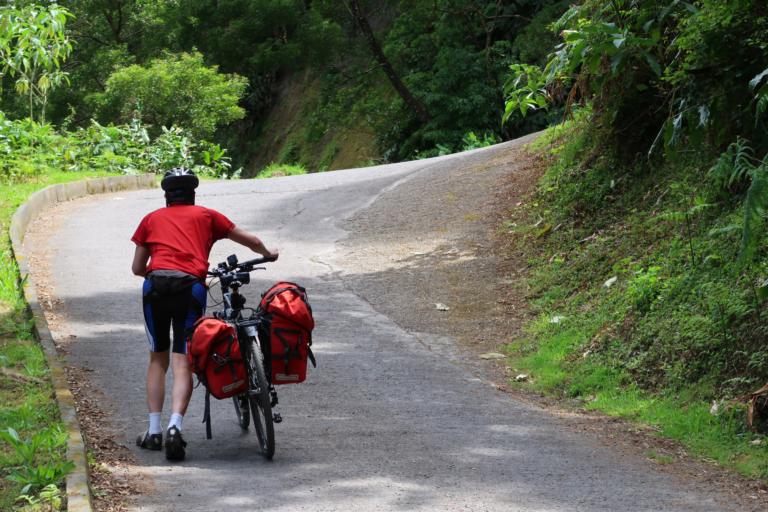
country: PT
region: Azores
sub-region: Ribeira Grande
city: Rabo de Peixe
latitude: 37.7957
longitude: -25.4971
